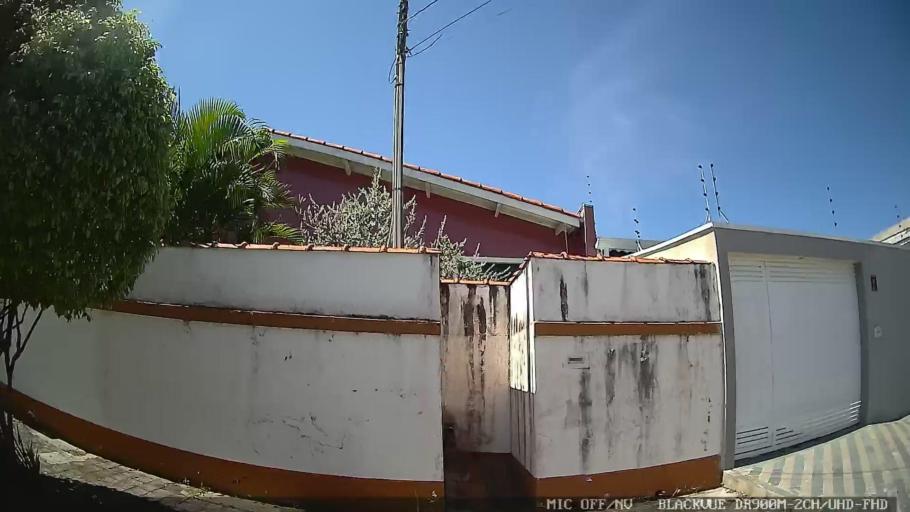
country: BR
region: Sao Paulo
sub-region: Peruibe
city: Peruibe
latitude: -24.3030
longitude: -46.9845
